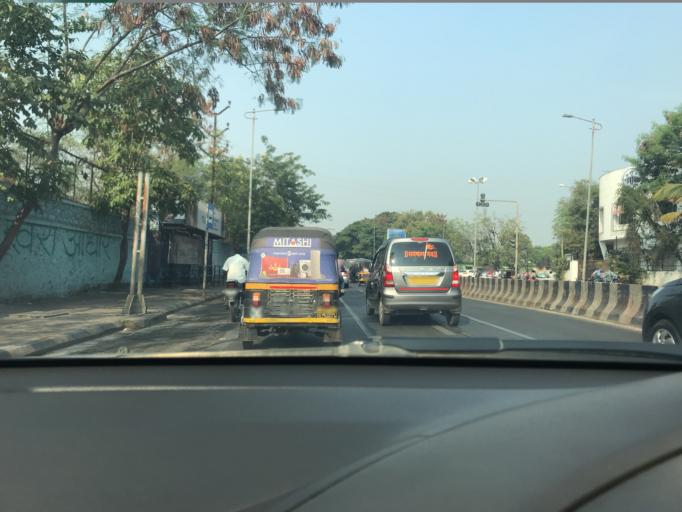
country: IN
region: Maharashtra
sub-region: Pune Division
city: Khadki
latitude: 18.5497
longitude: 73.8102
